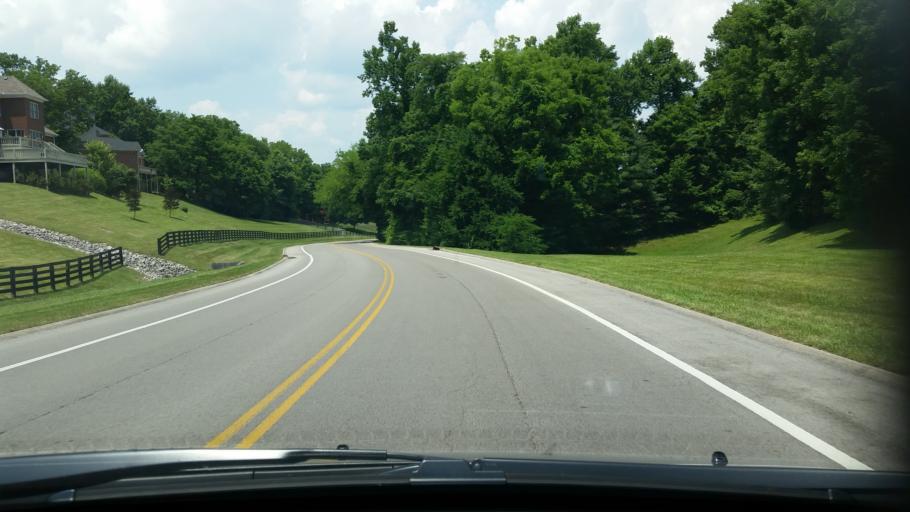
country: US
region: Tennessee
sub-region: Williamson County
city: Brentwood Estates
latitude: 35.9856
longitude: -86.7520
